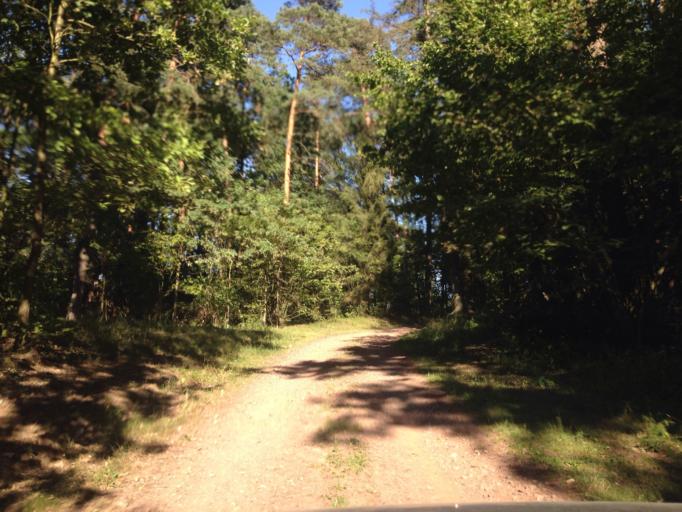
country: PL
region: Kujawsko-Pomorskie
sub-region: Powiat brodnicki
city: Gorzno
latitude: 53.1598
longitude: 19.6423
